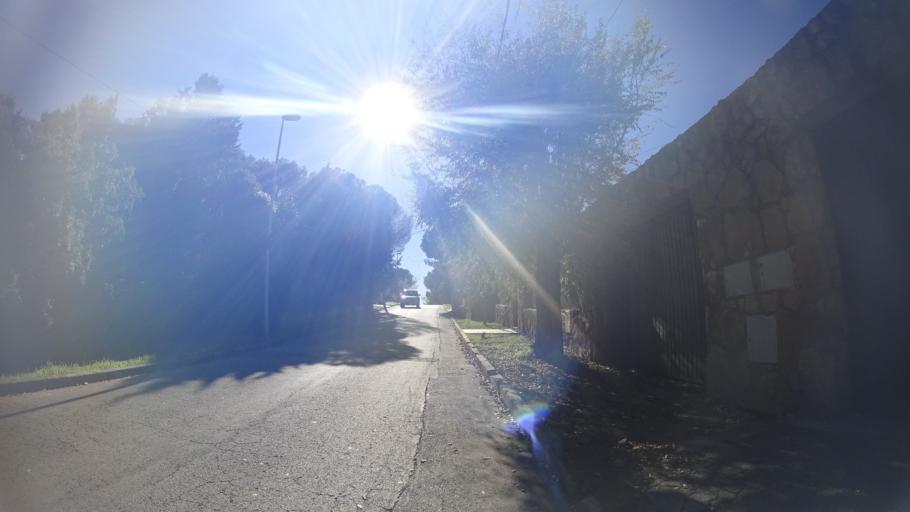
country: ES
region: Madrid
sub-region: Provincia de Madrid
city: Torrelodones
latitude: 40.5911
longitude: -3.9514
